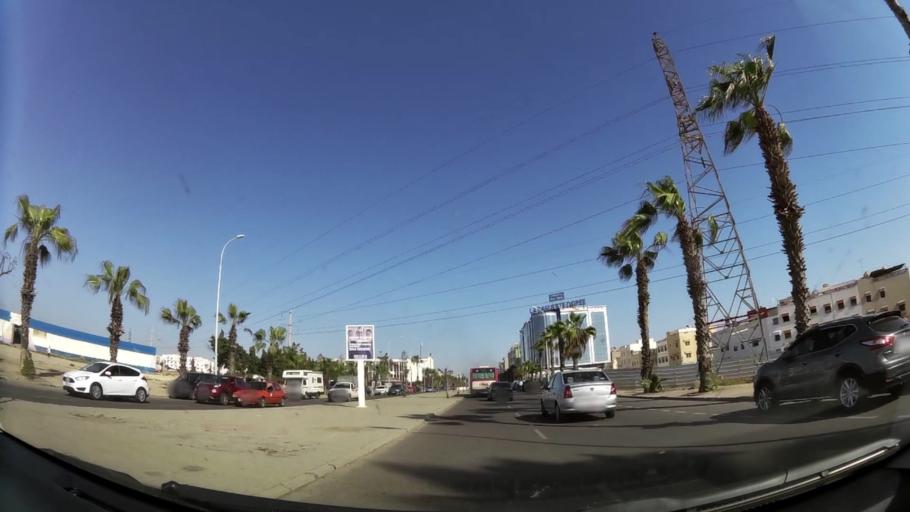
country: MA
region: Oued ed Dahab-Lagouira
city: Dakhla
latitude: 30.4141
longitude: -9.5684
